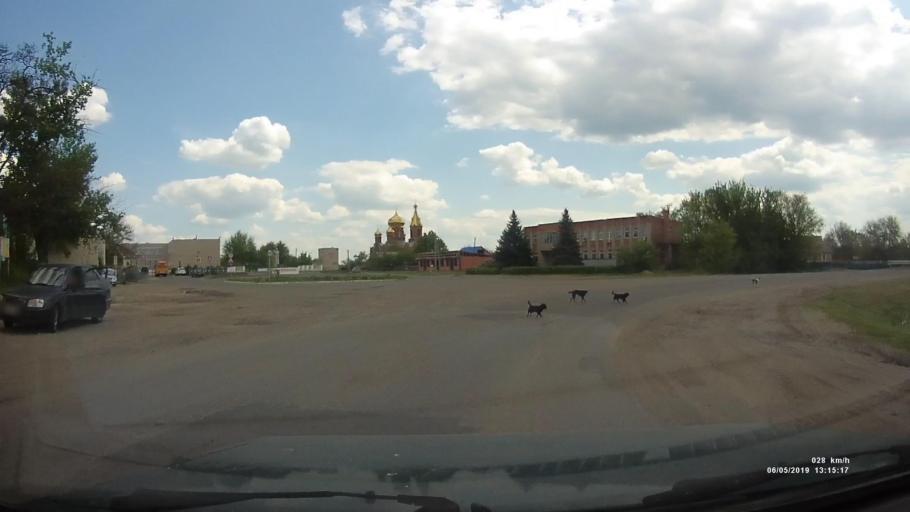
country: RU
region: Rostov
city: Ust'-Donetskiy
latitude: 47.7462
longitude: 40.9447
